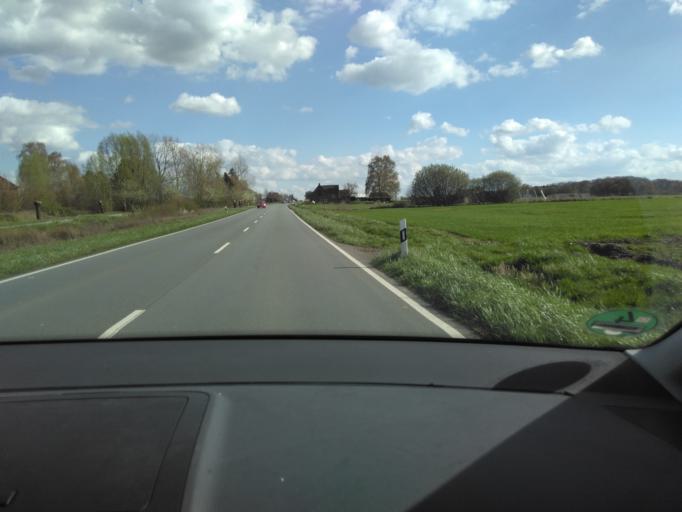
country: DE
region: North Rhine-Westphalia
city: Oelde
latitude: 51.7946
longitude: 8.1387
